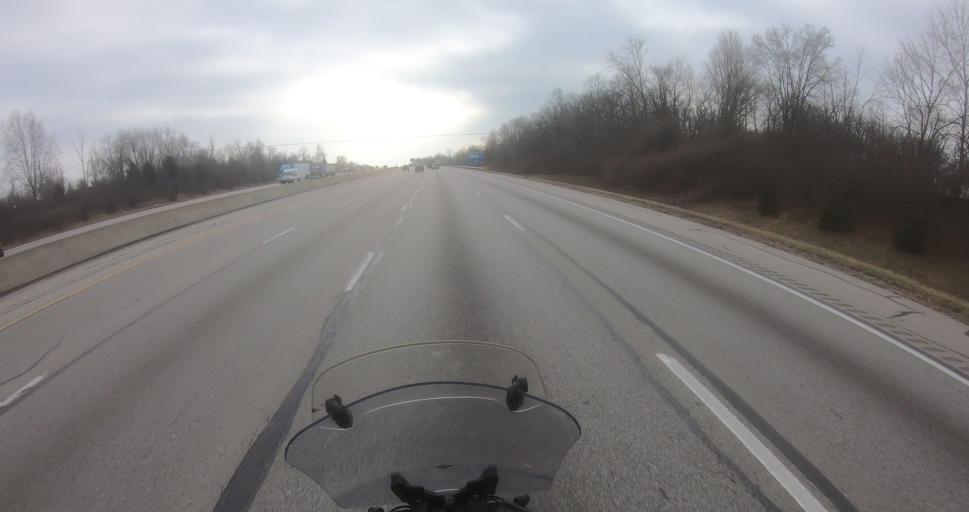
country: US
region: Ohio
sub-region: Warren County
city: Hunter
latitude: 39.5154
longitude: -84.3213
